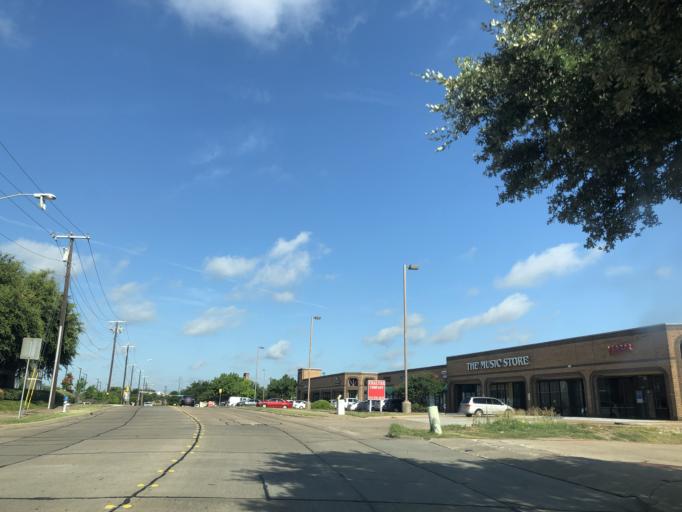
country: US
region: Texas
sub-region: Dallas County
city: Garland
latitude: 32.8594
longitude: -96.6459
